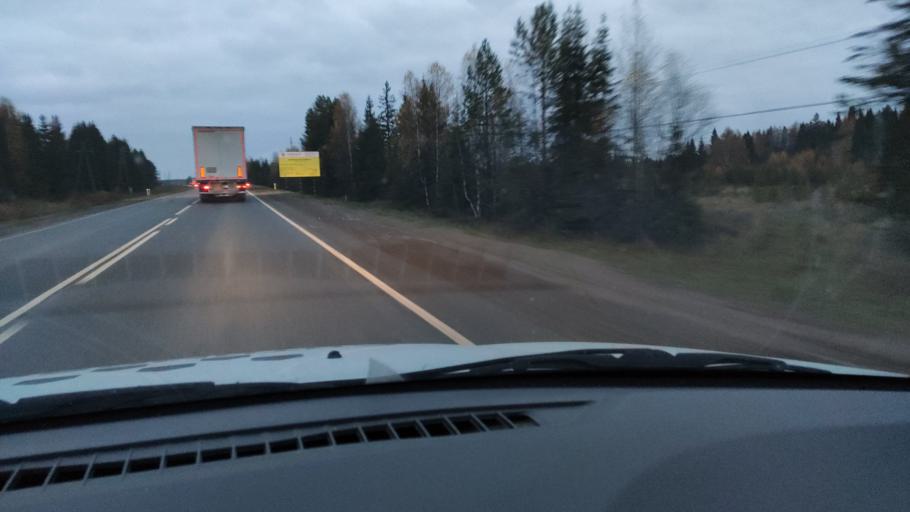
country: RU
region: Kirov
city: Kostino
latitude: 58.8365
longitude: 53.3044
